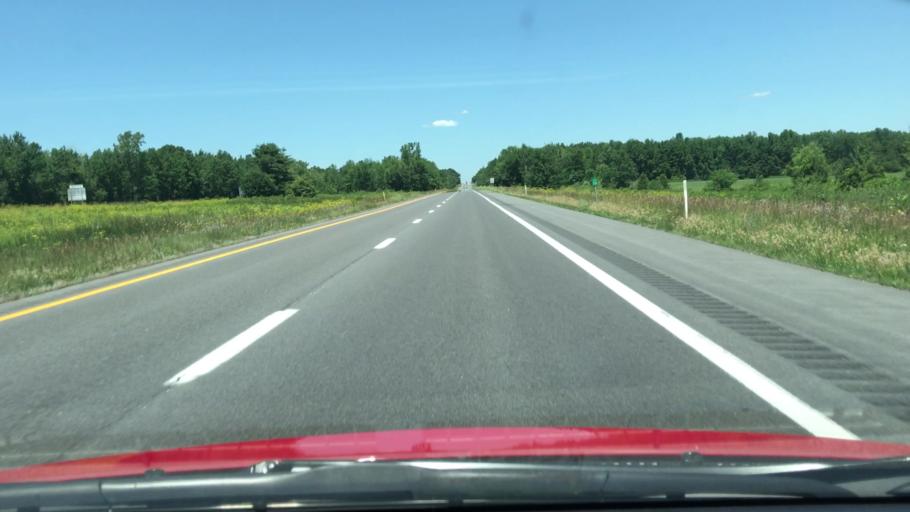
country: US
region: New York
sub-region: Clinton County
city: Cumberland Head
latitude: 44.7902
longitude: -73.4398
